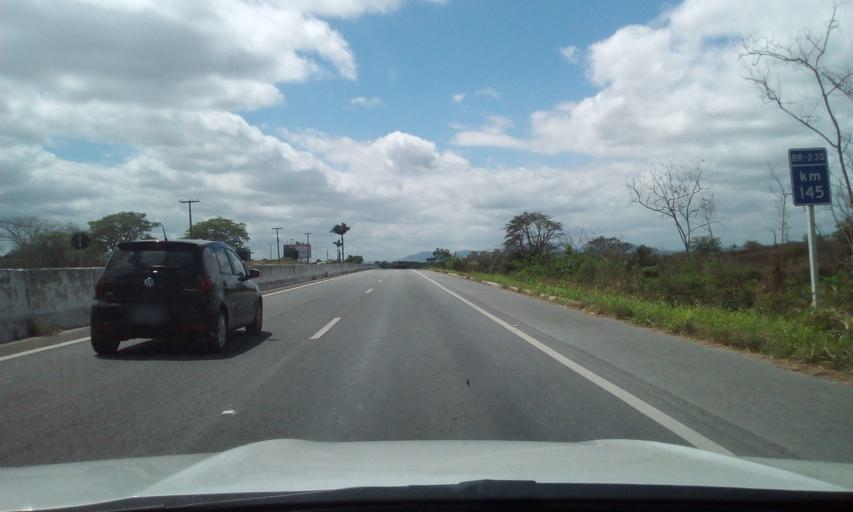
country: BR
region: Paraiba
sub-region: Campina Grande
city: Campina Grande
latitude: -7.2495
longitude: -35.8434
